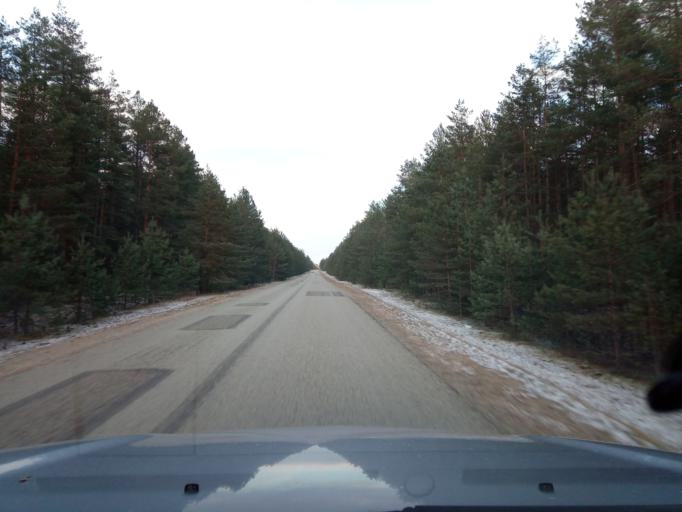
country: LT
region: Alytaus apskritis
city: Varena
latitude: 54.1391
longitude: 24.4721
